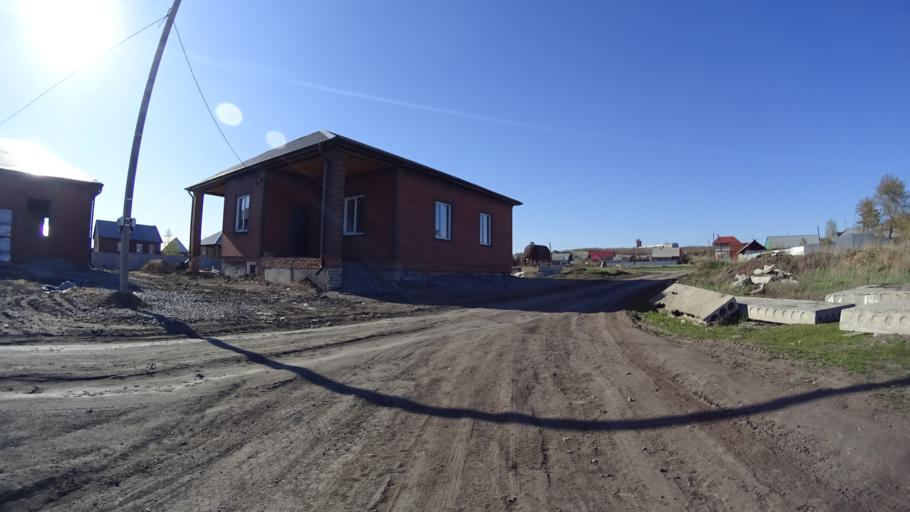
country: RU
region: Chelyabinsk
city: Troitsk
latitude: 54.0950
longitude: 61.5986
